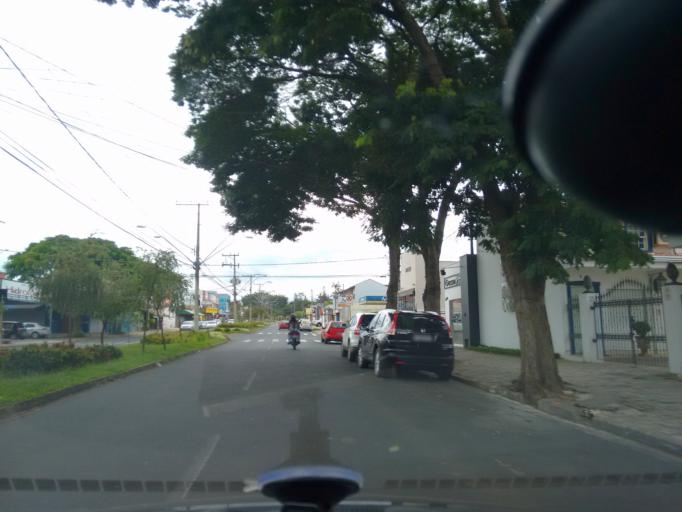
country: BR
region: Sao Paulo
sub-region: Indaiatuba
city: Indaiatuba
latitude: -23.0847
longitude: -47.2010
